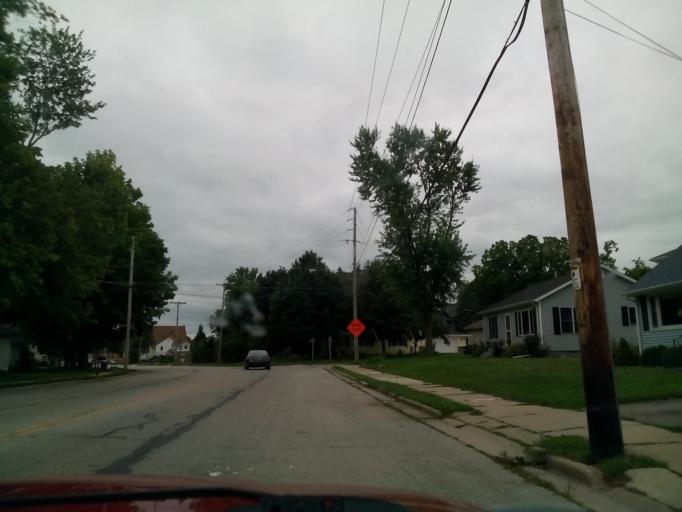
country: US
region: Wisconsin
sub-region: Outagamie County
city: Hortonville
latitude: 44.3381
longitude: -88.6364
